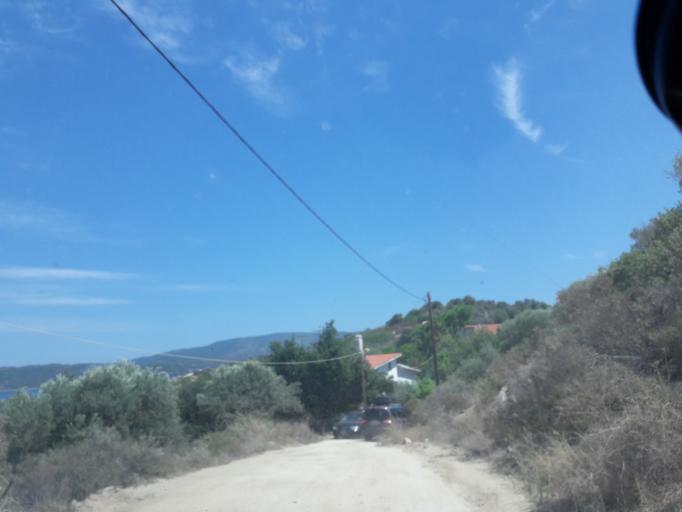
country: GR
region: Central Macedonia
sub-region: Nomos Chalkidikis
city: Ouranoupolis
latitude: 40.3164
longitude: 23.9325
